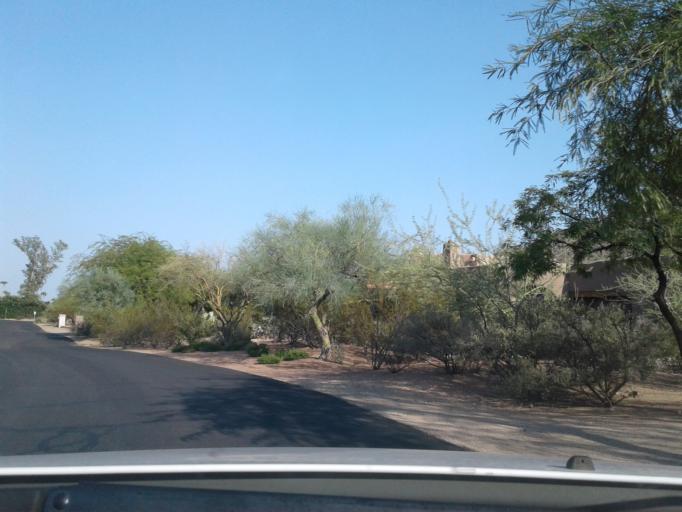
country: US
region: Arizona
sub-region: Maricopa County
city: Paradise Valley
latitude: 33.5251
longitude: -111.9667
